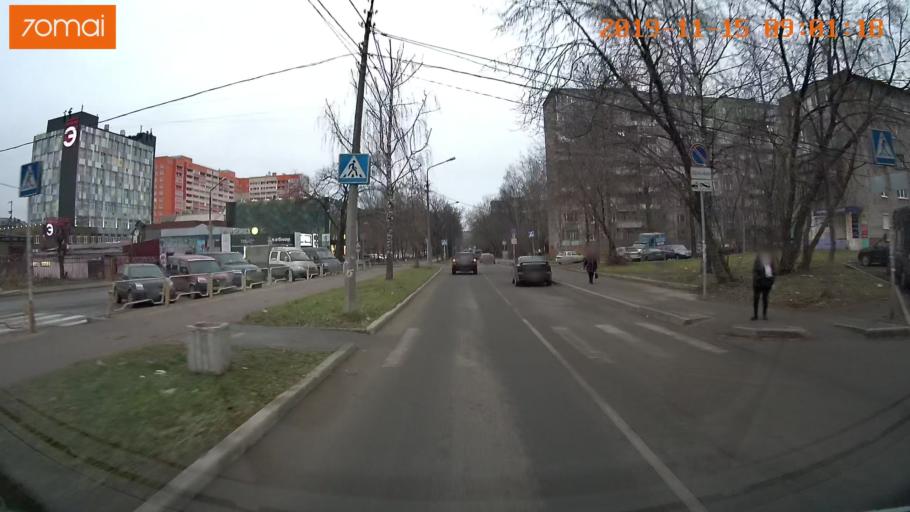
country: RU
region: Vologda
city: Cherepovets
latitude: 59.1317
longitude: 37.9256
